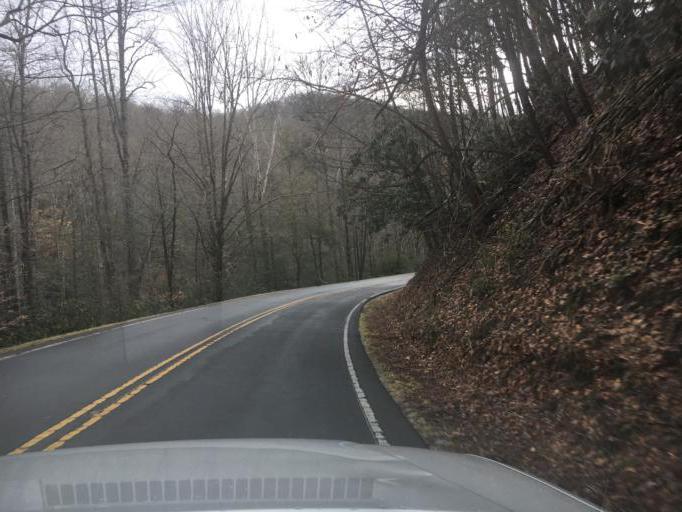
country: US
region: North Carolina
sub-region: Transylvania County
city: Brevard
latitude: 35.2825
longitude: -82.7532
